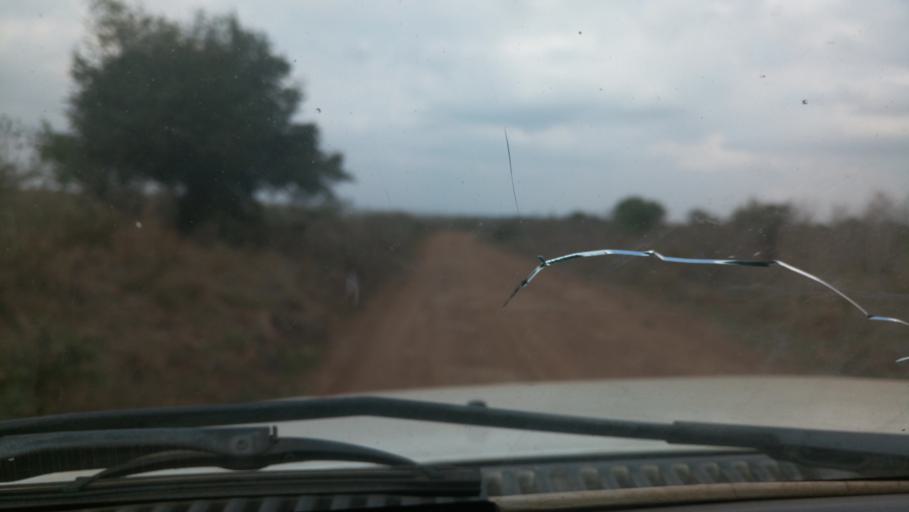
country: KE
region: Nairobi Area
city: Pumwani
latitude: -1.3716
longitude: 36.8347
